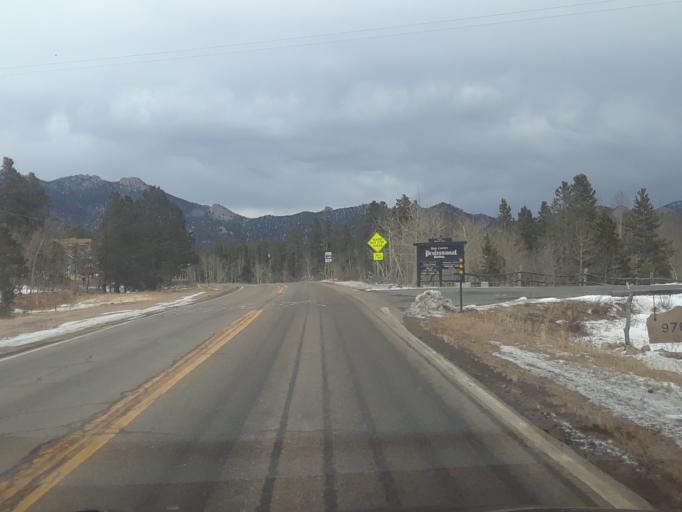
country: US
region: Colorado
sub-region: Gilpin County
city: Central City
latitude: 39.8386
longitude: -105.4770
